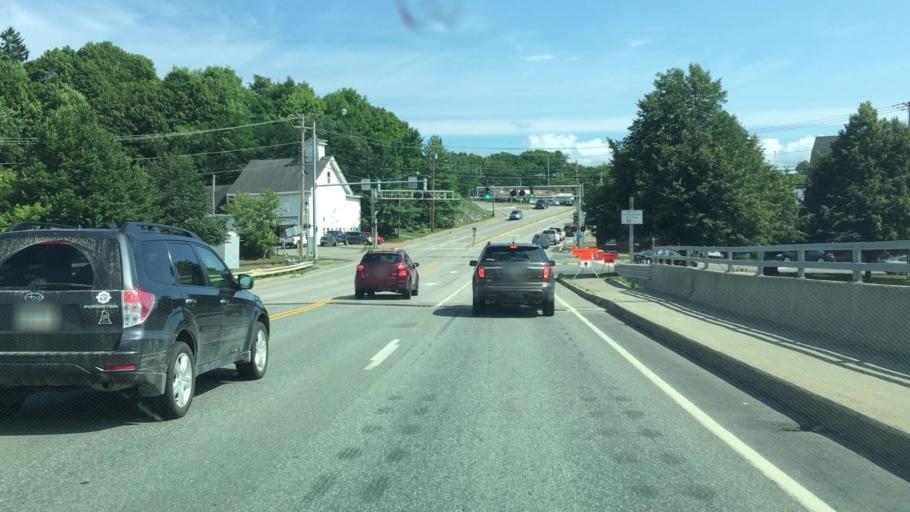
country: US
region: Maine
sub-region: Penobscot County
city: Brewer
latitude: 44.7984
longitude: -68.7632
